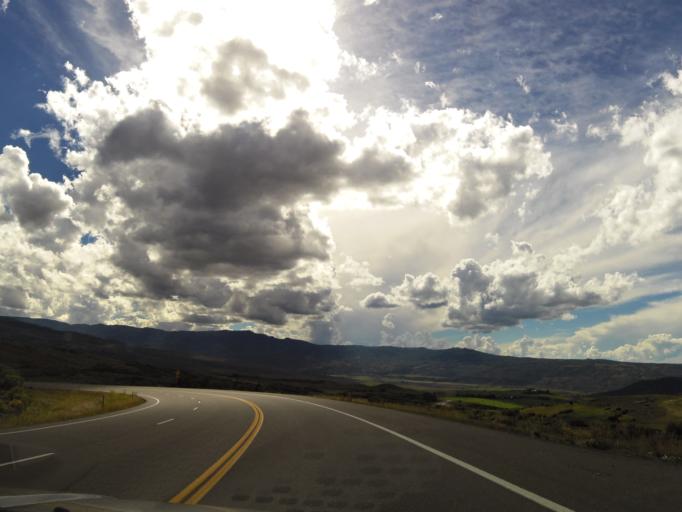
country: US
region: Colorado
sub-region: Hinsdale County
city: Lake City
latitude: 38.3970
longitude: -107.4531
